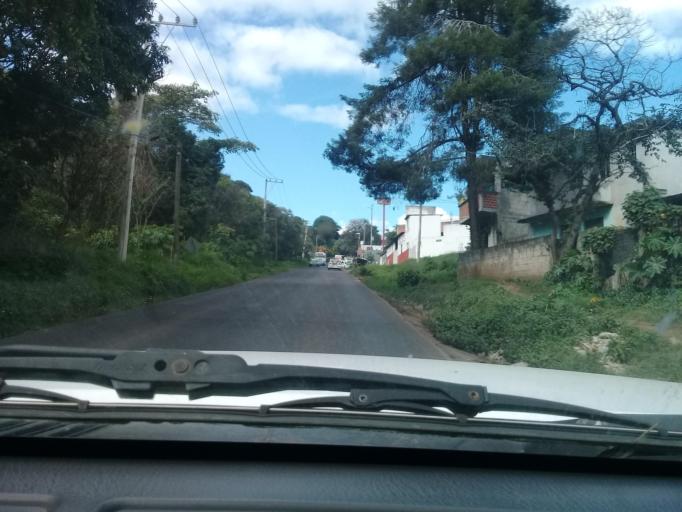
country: MX
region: Veracruz
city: El Castillo
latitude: 19.5468
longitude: -96.8842
